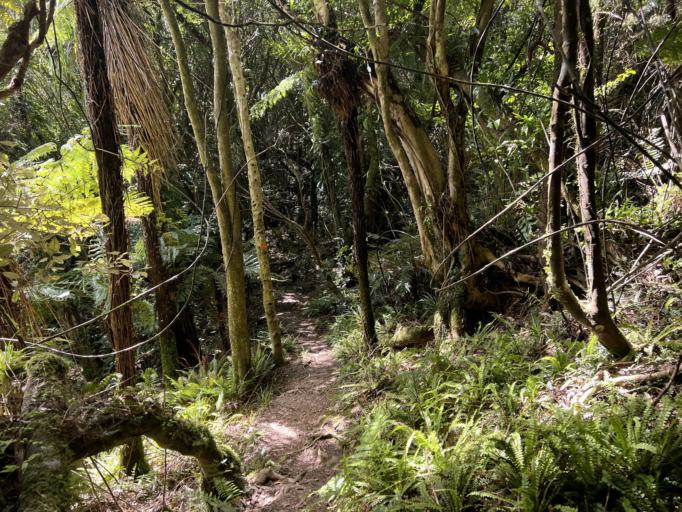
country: NZ
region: Wellington
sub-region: Kapiti Coast District
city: Paraparaumu
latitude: -40.8807
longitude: 175.0898
